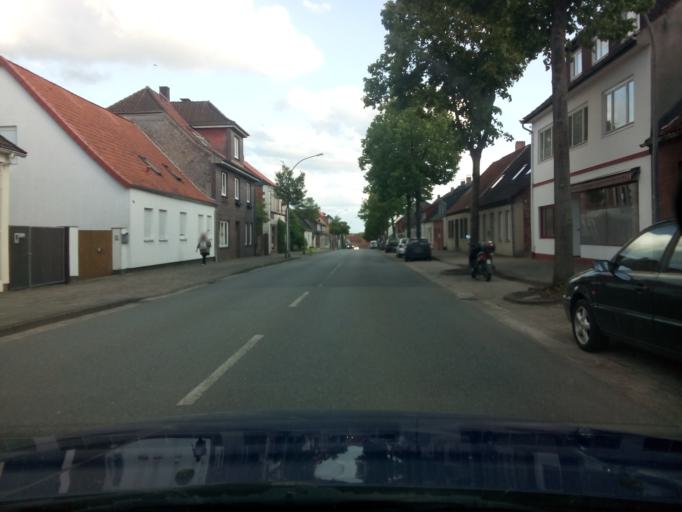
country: DE
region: Lower Saxony
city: Walsrode
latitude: 52.8670
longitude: 9.5859
